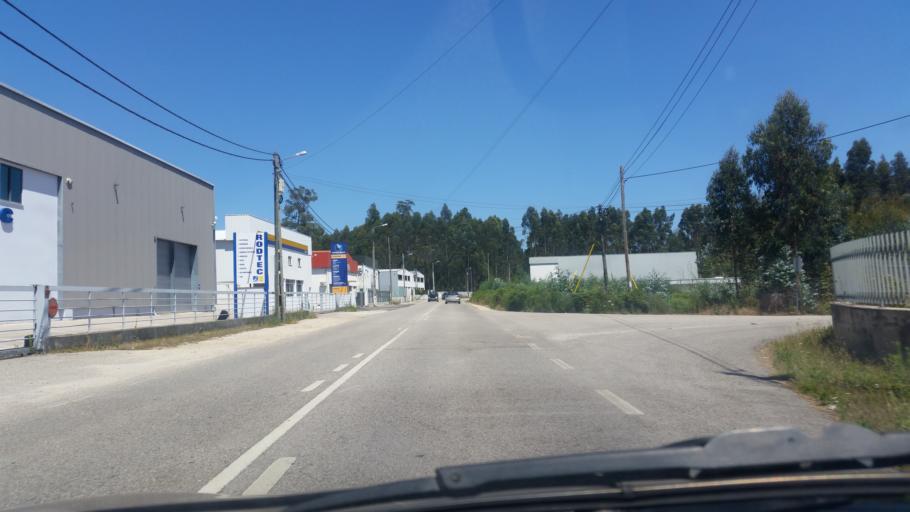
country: PT
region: Aveiro
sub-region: Agueda
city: Valongo
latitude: 40.5950
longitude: -8.4899
